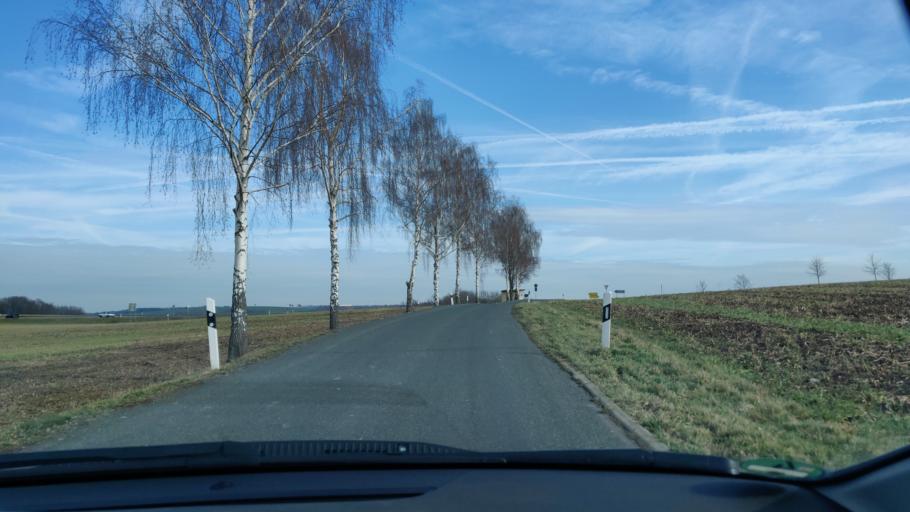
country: DE
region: Saxony
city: Rochlitz
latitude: 51.0674
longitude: 12.7789
